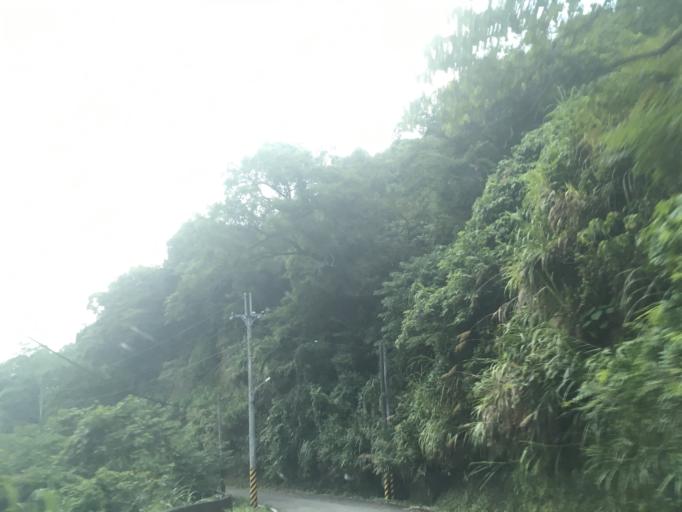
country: TW
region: Taiwan
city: Fengyuan
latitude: 24.1875
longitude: 120.7814
